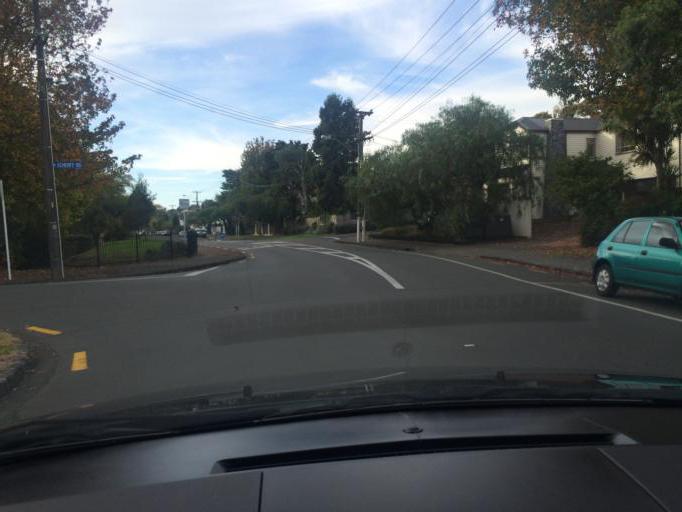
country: NZ
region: Auckland
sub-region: Auckland
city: Auckland
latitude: -36.8703
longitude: 174.7959
